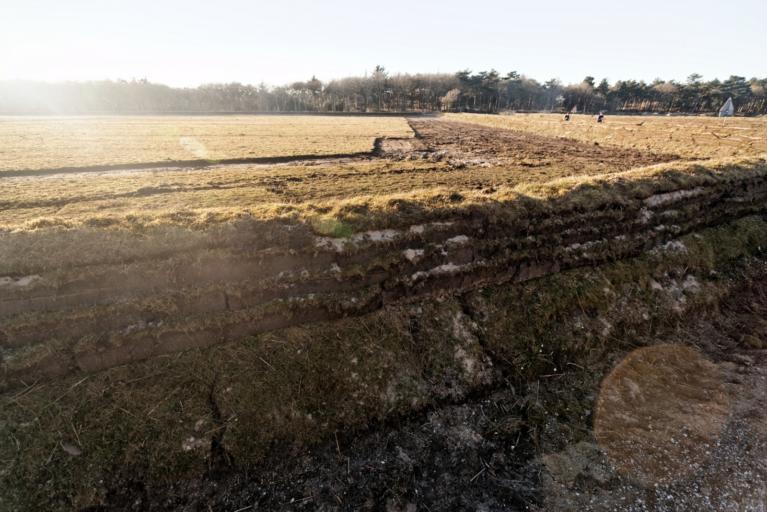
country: NL
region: North Holland
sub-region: Gemeente Texel
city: Den Burg
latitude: 53.0832
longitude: 4.7532
